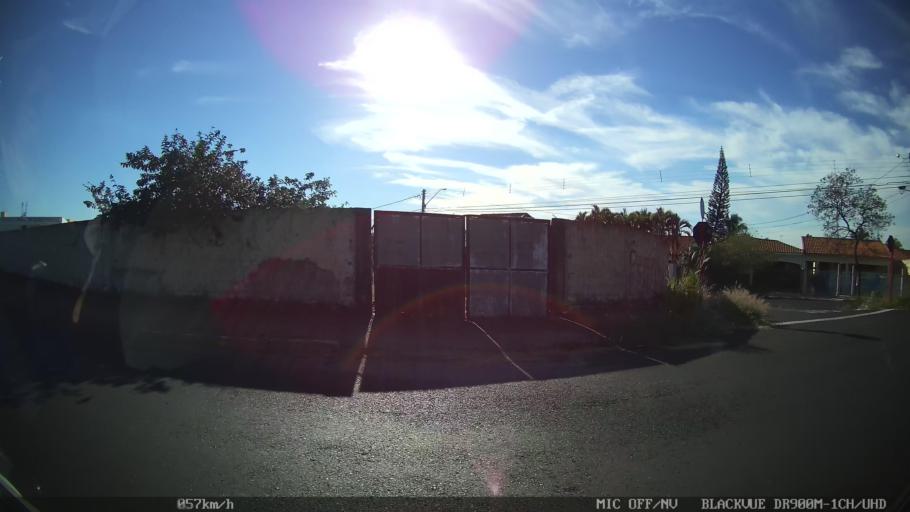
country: BR
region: Sao Paulo
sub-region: Araraquara
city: Araraquara
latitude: -21.7656
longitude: -48.1606
